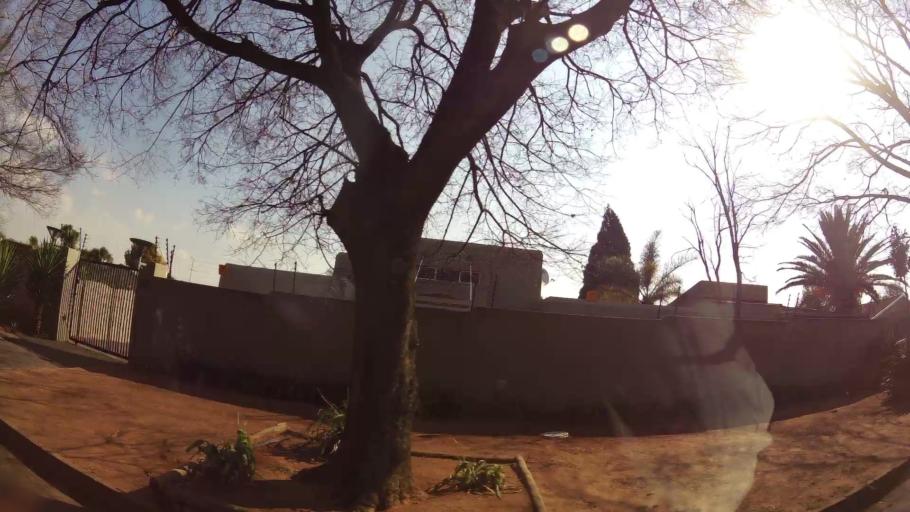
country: ZA
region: Gauteng
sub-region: Ekurhuleni Metropolitan Municipality
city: Boksburg
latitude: -26.1883
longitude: 28.2658
